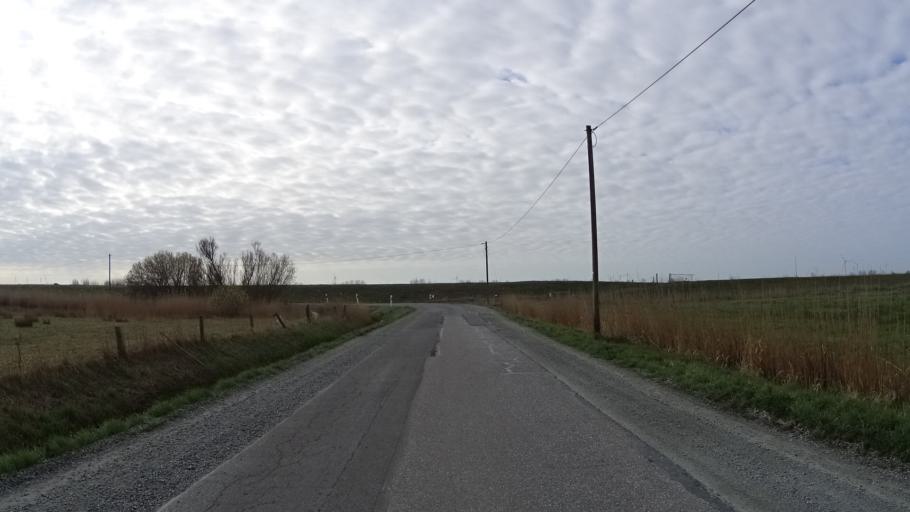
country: DE
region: Lower Saxony
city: Emden
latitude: 53.4032
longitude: 7.3196
